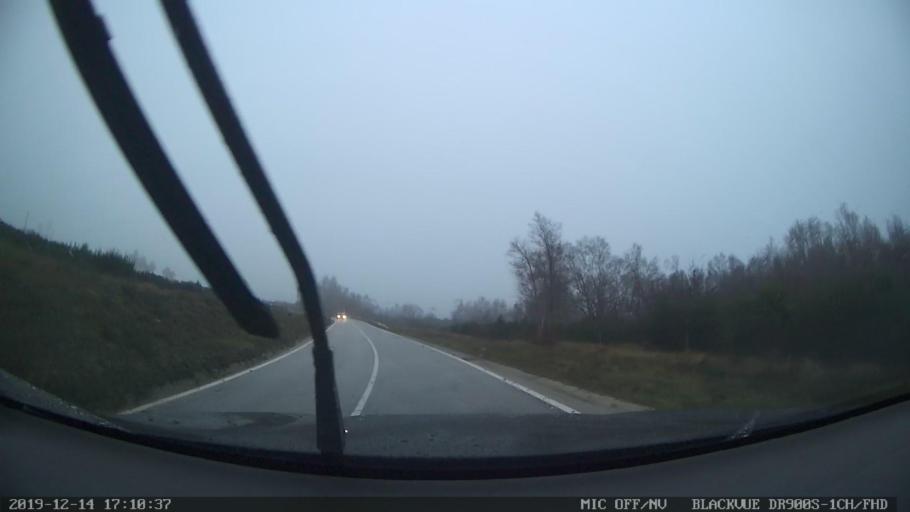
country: PT
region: Vila Real
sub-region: Vila Pouca de Aguiar
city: Vila Pouca de Aguiar
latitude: 41.4819
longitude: -7.6102
